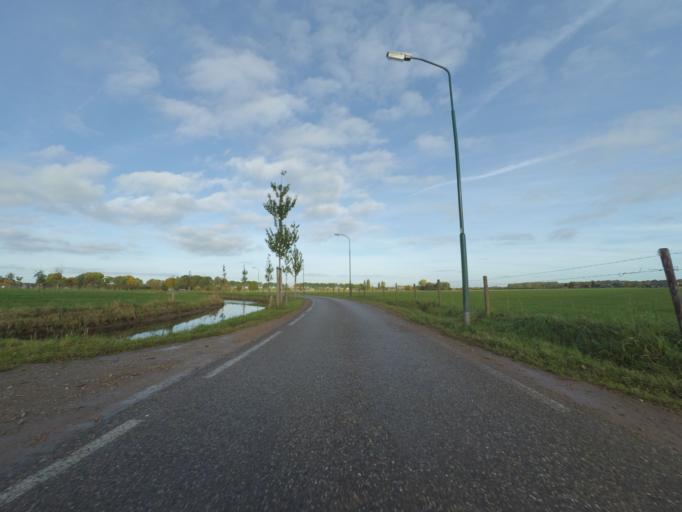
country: NL
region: Utrecht
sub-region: Gemeente Utrechtse Heuvelrug
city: Driebergen-Rijsenburg
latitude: 51.9967
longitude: 5.2782
